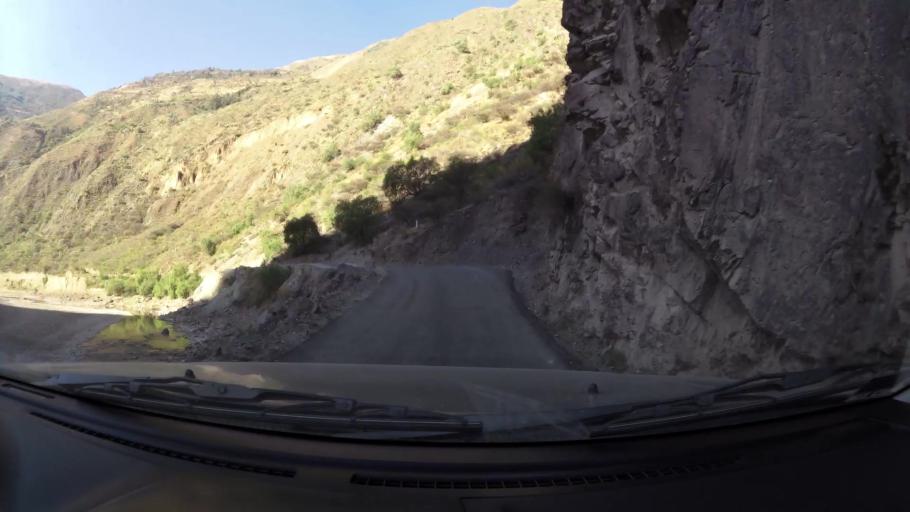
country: PE
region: Huancavelica
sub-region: Provincia de Churcampa
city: La Esmeralda
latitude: -12.5761
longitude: -74.6905
